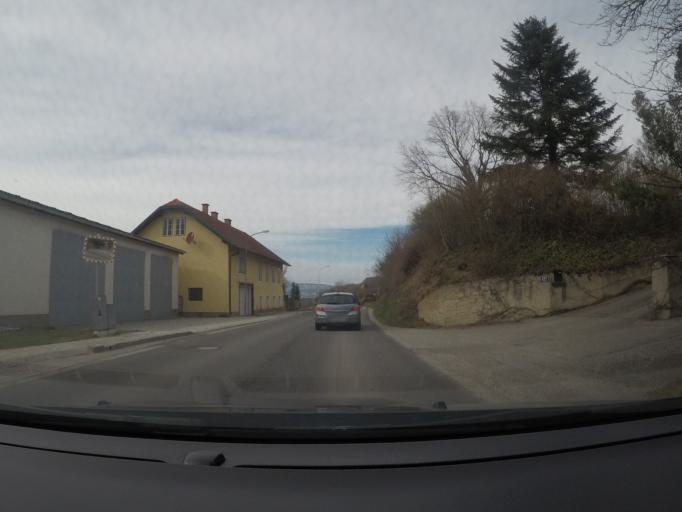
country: AT
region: Lower Austria
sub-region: Politischer Bezirk Neunkirchen
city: Pitten
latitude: 47.7242
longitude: 16.1792
